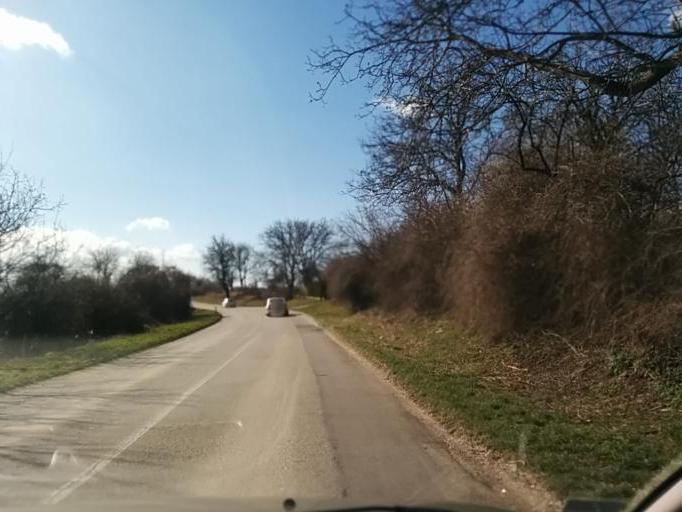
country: SK
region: Trenciansky
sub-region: Okres Nove Mesto nad Vahom
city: Nove Mesto nad Vahom
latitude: 48.7331
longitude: 17.8129
